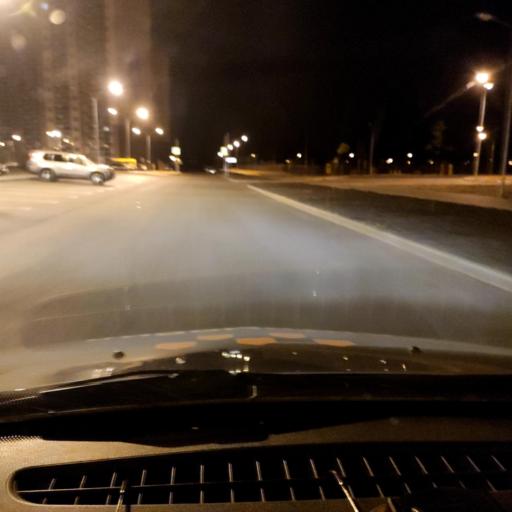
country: RU
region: Voronezj
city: Shilovo
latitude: 51.5670
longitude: 39.1215
